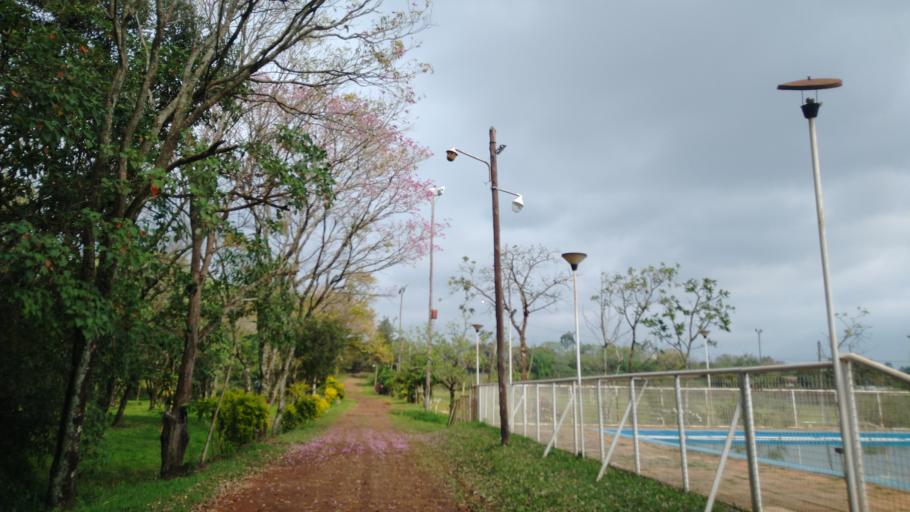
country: AR
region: Misiones
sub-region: Departamento de Capital
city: Posadas
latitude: -27.4095
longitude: -55.9399
